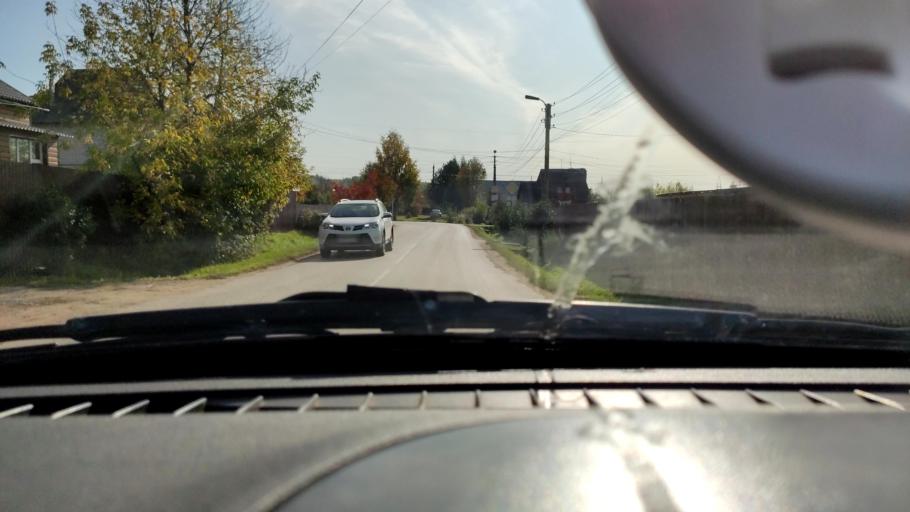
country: RU
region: Perm
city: Overyata
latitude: 58.0820
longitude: 55.8798
